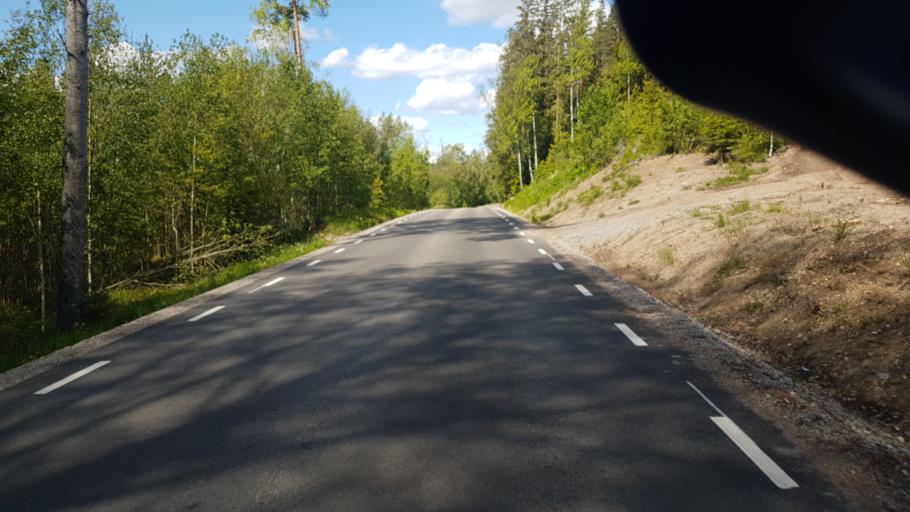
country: SE
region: Vaermland
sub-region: Arvika Kommun
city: Arvika
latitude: 59.6567
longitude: 12.8026
